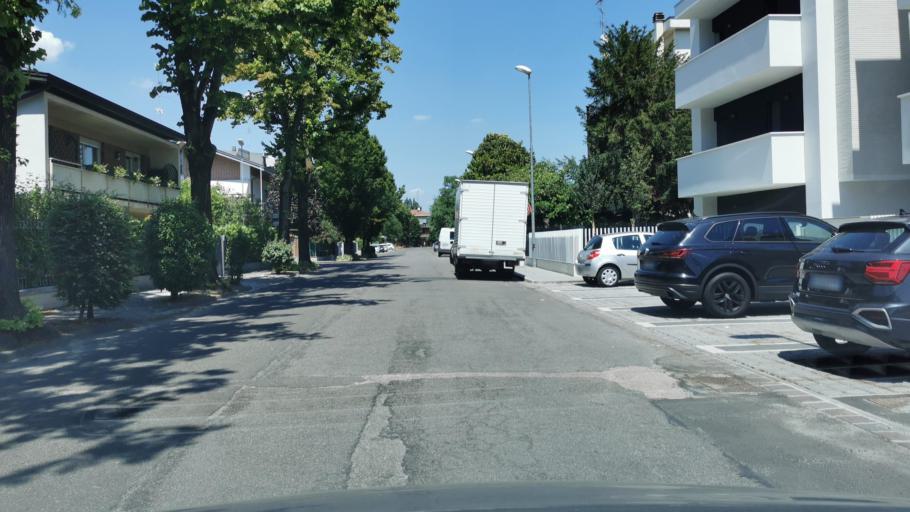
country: IT
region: Emilia-Romagna
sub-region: Provincia di Modena
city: Carpi Centro
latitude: 44.7894
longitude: 10.8864
